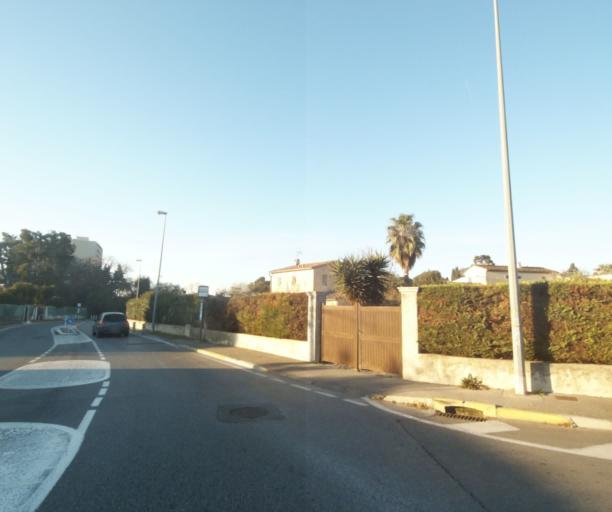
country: FR
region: Provence-Alpes-Cote d'Azur
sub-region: Departement des Alpes-Maritimes
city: Vallauris
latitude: 43.5788
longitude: 7.0886
